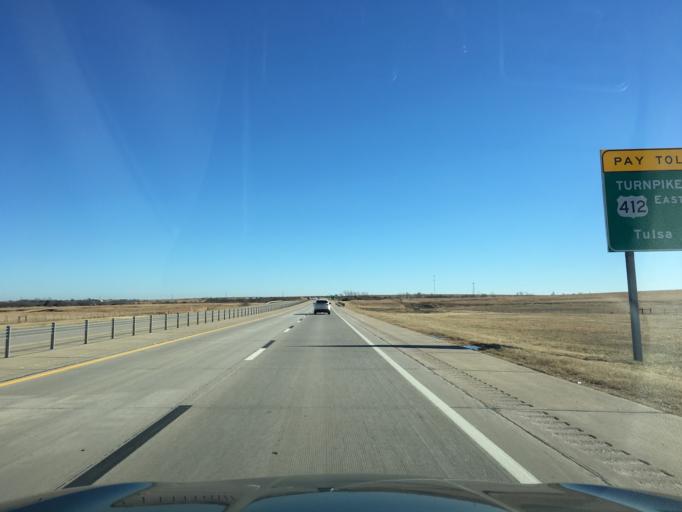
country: US
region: Oklahoma
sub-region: Noble County
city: Perry
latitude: 36.3893
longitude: -97.0952
